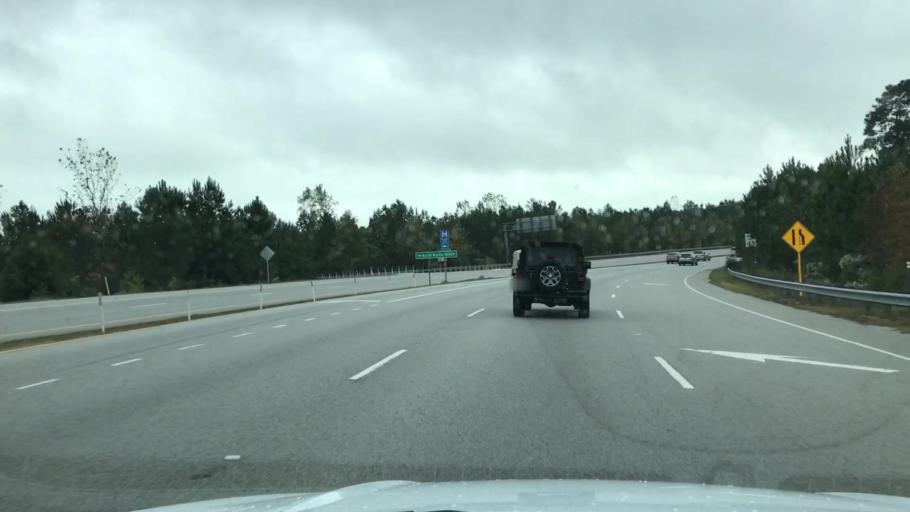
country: US
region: South Carolina
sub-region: Horry County
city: Myrtle Beach
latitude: 33.7384
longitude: -78.8503
